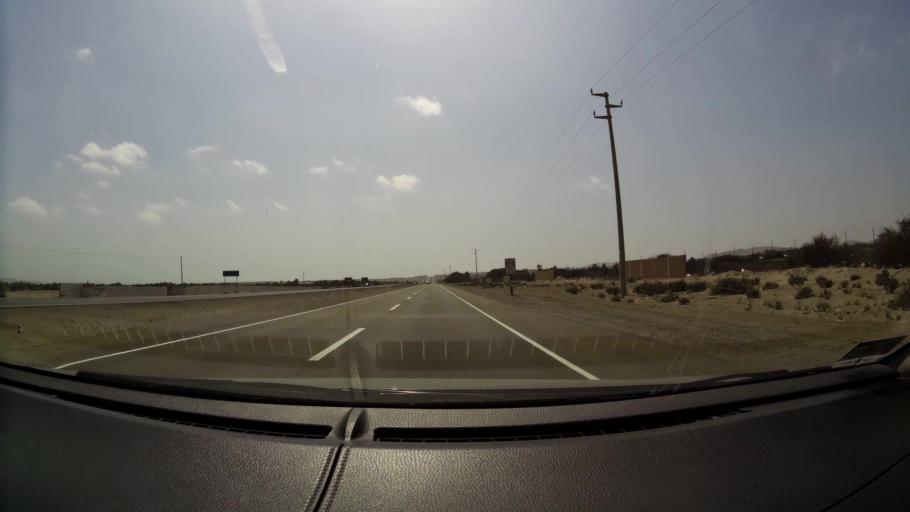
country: PE
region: Lima
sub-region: Huaura
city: Huacho
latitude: -11.2139
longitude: -77.5551
